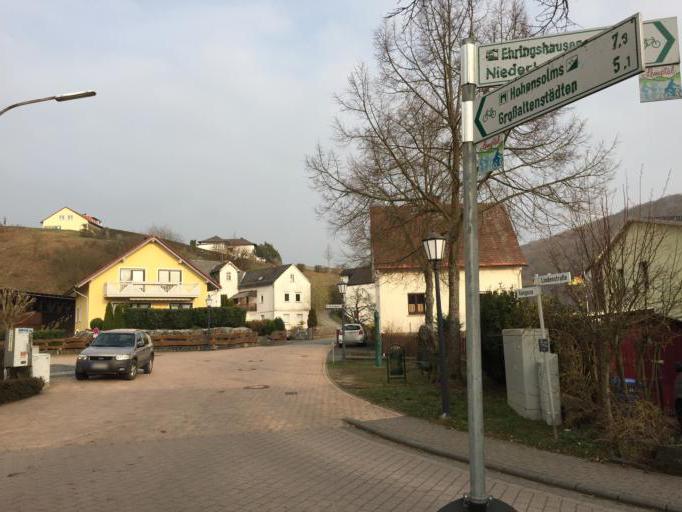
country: DE
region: Hesse
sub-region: Regierungsbezirk Giessen
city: Bischoffen
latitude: 50.6472
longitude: 8.4391
